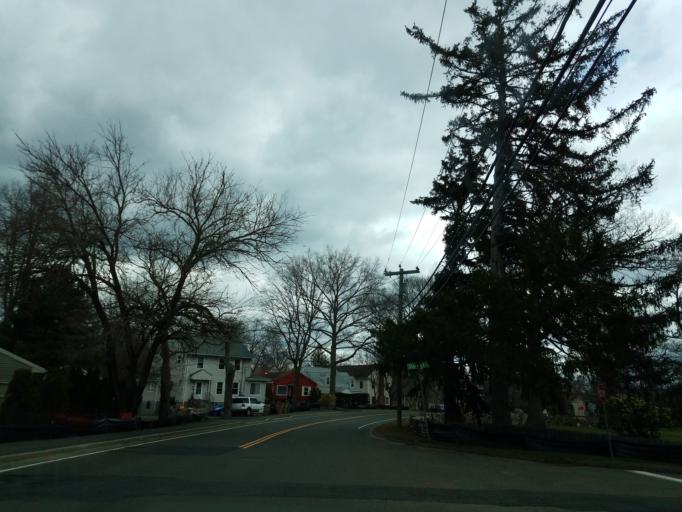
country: US
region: Connecticut
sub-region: Fairfield County
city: Stamford
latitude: 41.0773
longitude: -73.5451
